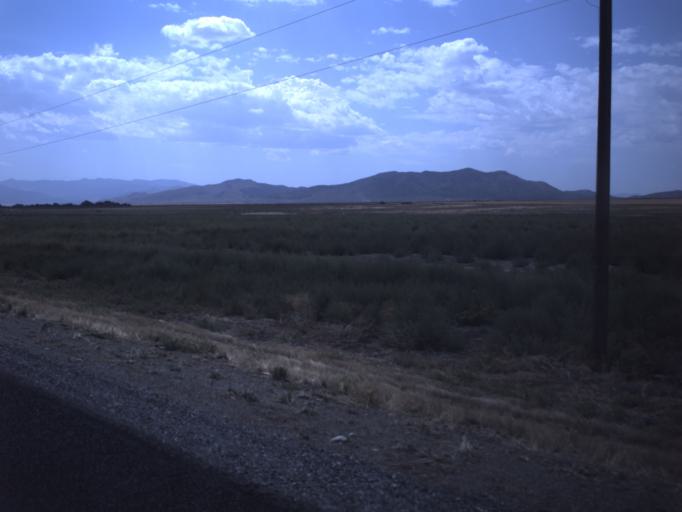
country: US
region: Utah
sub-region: Utah County
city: Eagle Mountain
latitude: 40.2793
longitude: -112.0952
